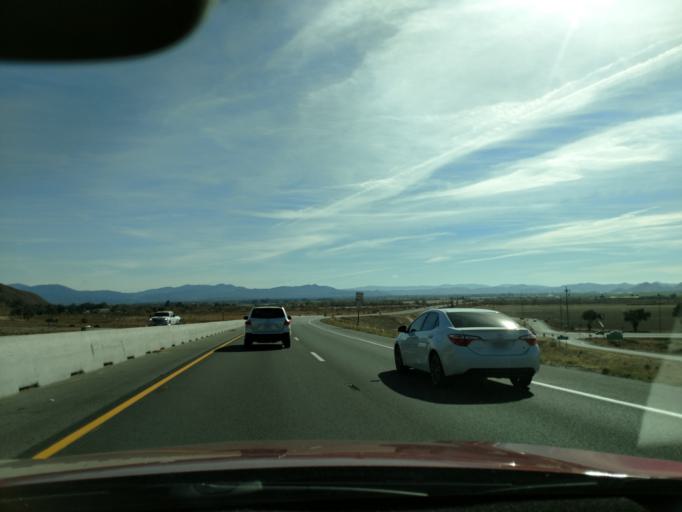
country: US
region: California
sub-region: Riverside County
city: San Jacinto
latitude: 33.8482
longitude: -117.0053
